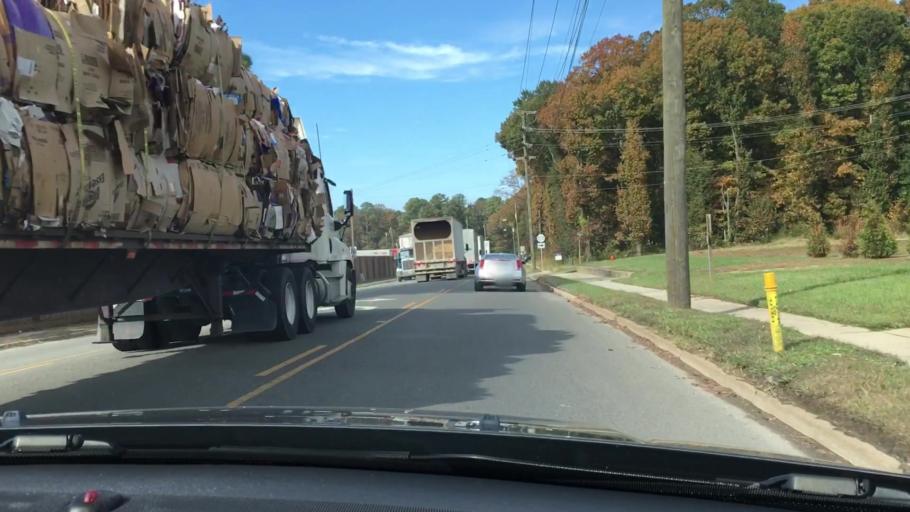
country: US
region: Virginia
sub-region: King William County
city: West Point
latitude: 37.5432
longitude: -76.8027
